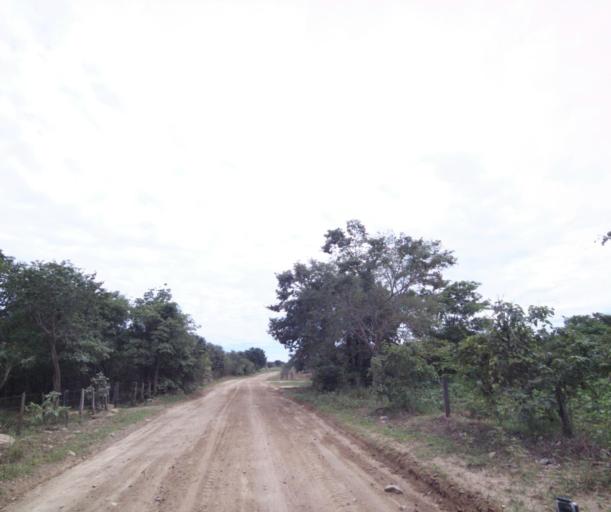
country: BR
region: Bahia
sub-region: Carinhanha
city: Carinhanha
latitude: -14.2244
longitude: -44.2992
